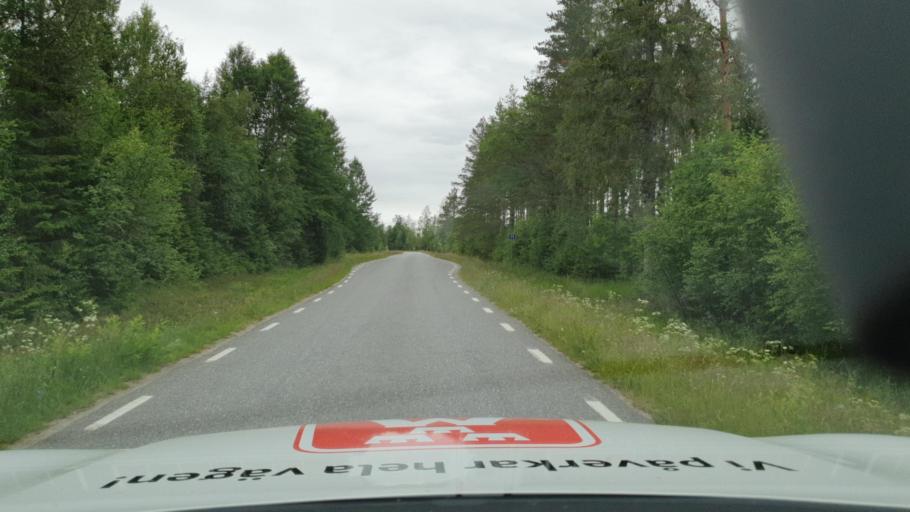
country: SE
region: Vaesterbotten
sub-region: Nordmalings Kommun
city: Nordmaling
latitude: 63.4940
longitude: 19.4353
